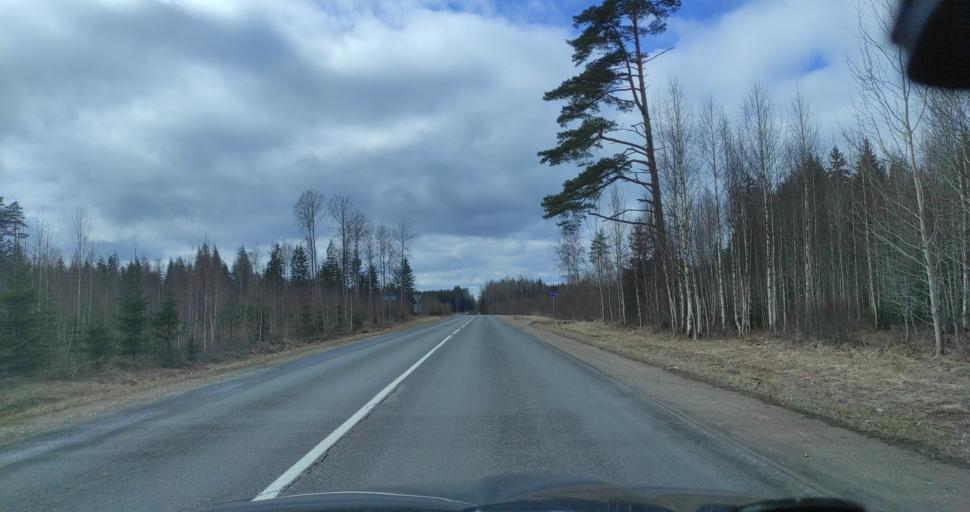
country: LV
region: Talsu Rajons
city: Stende
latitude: 57.1248
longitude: 22.5383
